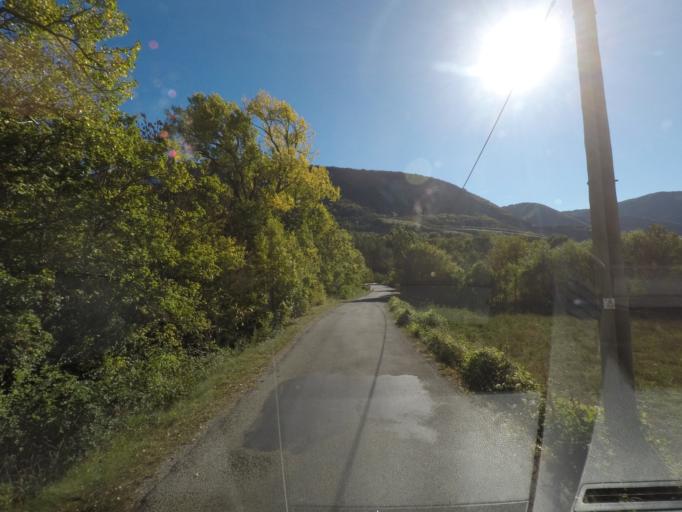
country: FR
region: Provence-Alpes-Cote d'Azur
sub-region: Departement des Hautes-Alpes
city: Serres
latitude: 44.4687
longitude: 5.5086
